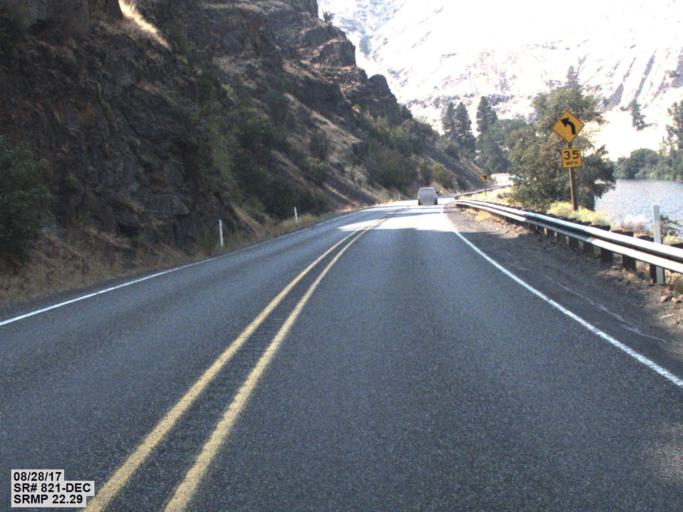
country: US
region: Washington
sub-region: Kittitas County
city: Ellensburg
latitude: 46.8981
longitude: -120.4974
